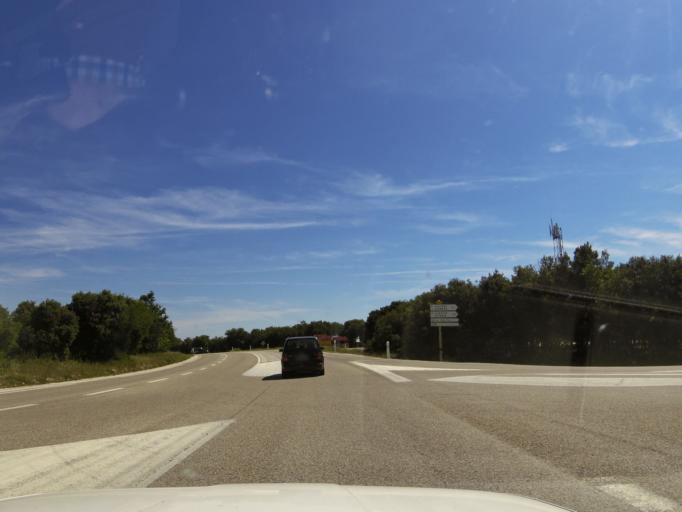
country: FR
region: Languedoc-Roussillon
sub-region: Departement du Gard
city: Saint-Quentin-la-Poterie
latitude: 44.1254
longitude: 4.4567
